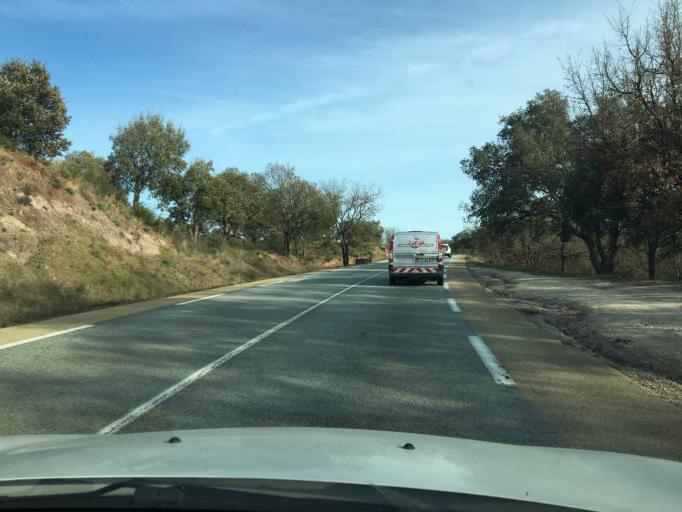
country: FR
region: Provence-Alpes-Cote d'Azur
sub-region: Departement du Var
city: Montauroux
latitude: 43.5487
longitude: 6.8030
